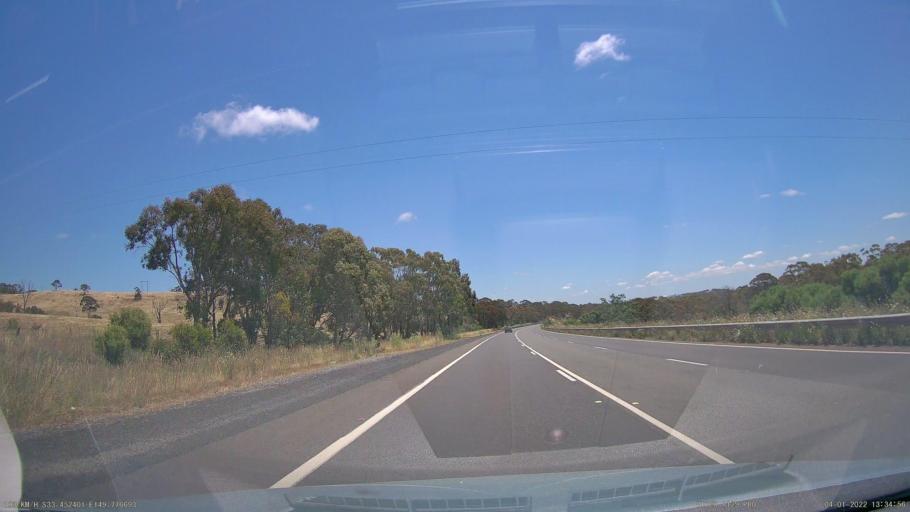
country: AU
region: New South Wales
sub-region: Bathurst Regional
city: Kelso
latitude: -33.4527
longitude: 149.7764
